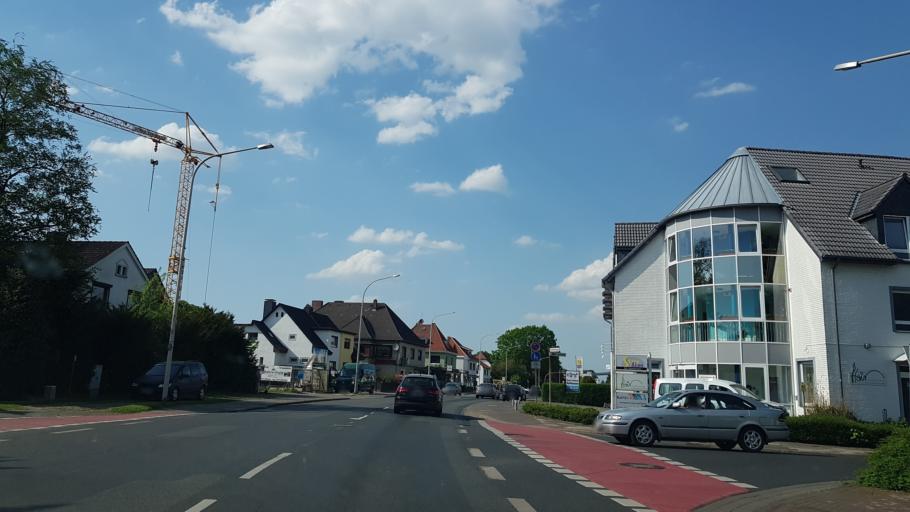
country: DE
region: Lower Saxony
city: Langen
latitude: 53.5963
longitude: 8.5964
